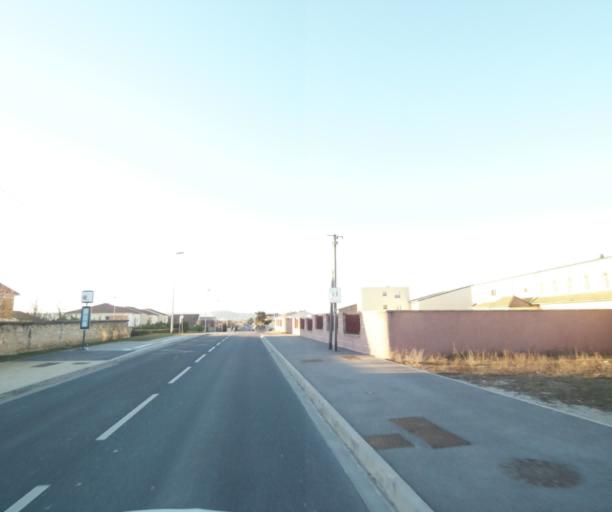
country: FR
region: Lorraine
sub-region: Departement de Meurthe-et-Moselle
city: Tomblaine
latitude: 48.6745
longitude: 6.2236
